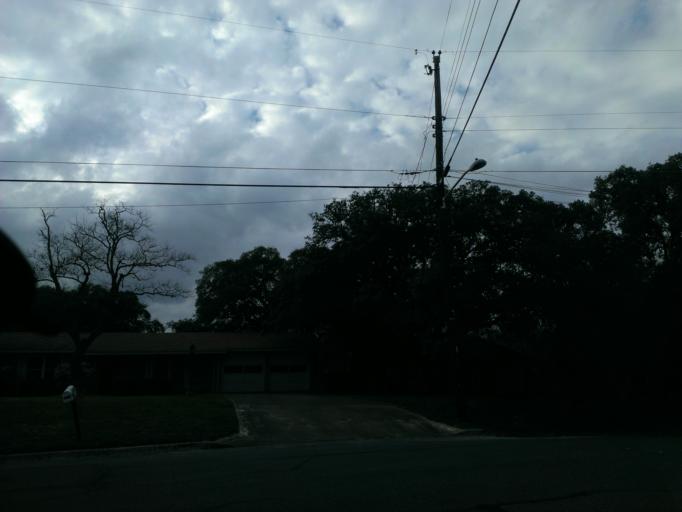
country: US
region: Texas
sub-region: Travis County
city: Wells Branch
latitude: 30.3842
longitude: -97.6813
